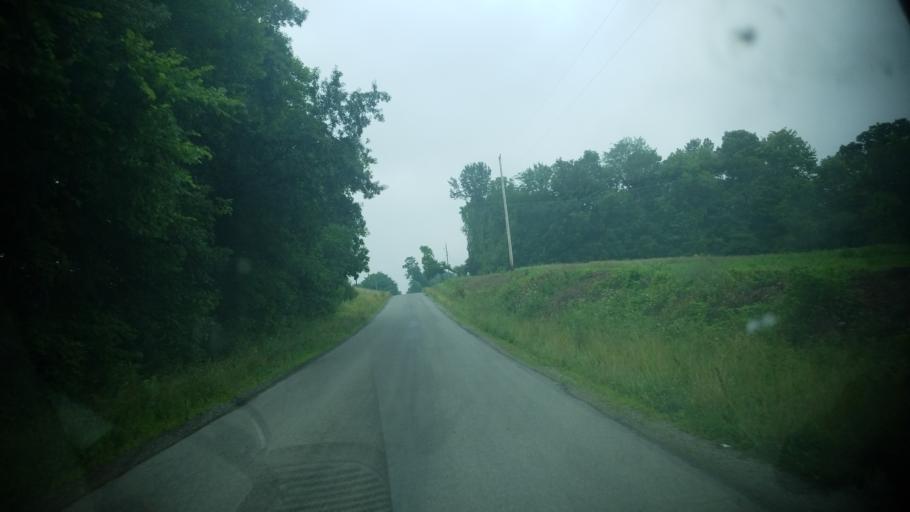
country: US
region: Illinois
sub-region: Clay County
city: Flora
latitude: 38.6726
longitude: -88.3548
